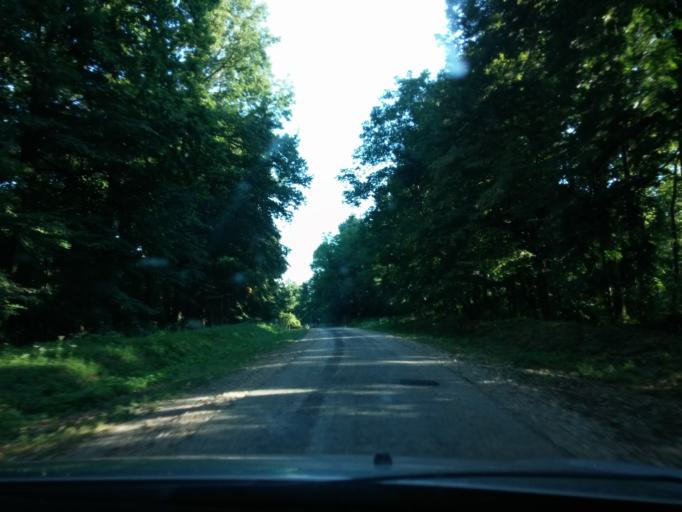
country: HU
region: Somogy
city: Kaposmero
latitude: 46.2453
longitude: 17.7578
